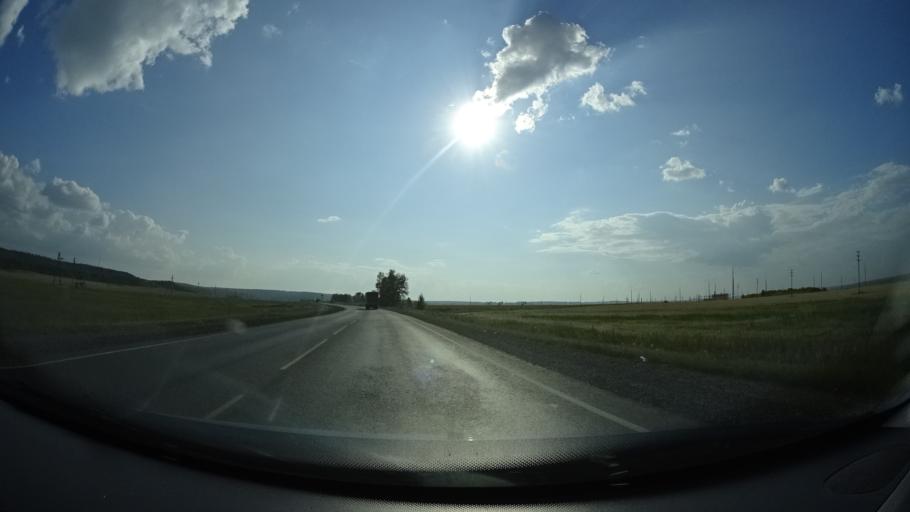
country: RU
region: Tatarstan
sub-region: Bavlinskiy Rayon
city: Bavly
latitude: 54.4741
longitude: 53.3159
